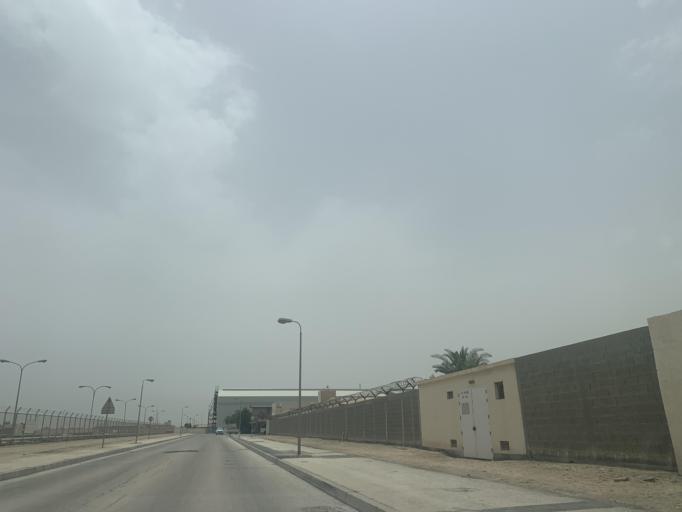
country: BH
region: Northern
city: Sitrah
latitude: 26.1813
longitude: 50.6127
